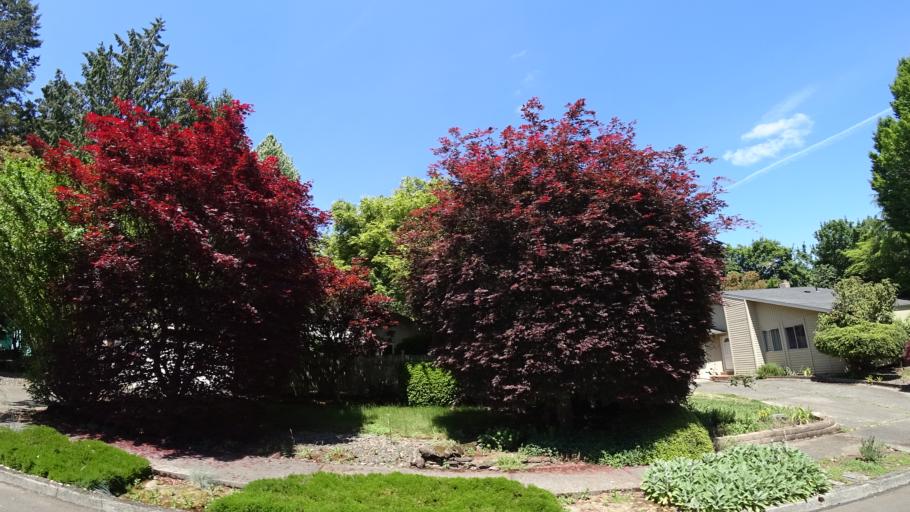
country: US
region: Oregon
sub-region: Washington County
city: King City
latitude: 45.4329
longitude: -122.8064
